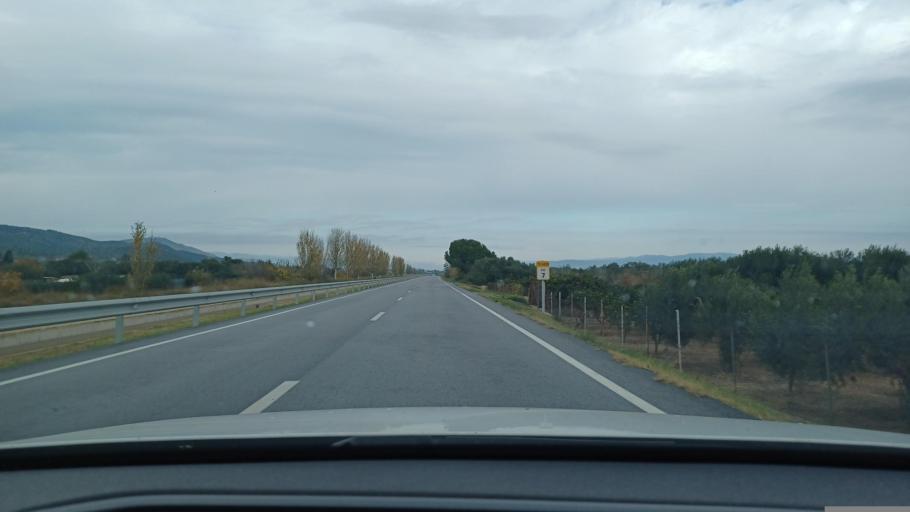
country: ES
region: Catalonia
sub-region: Provincia de Tarragona
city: Sant Carles de la Rapita
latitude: 40.6468
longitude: 0.5983
